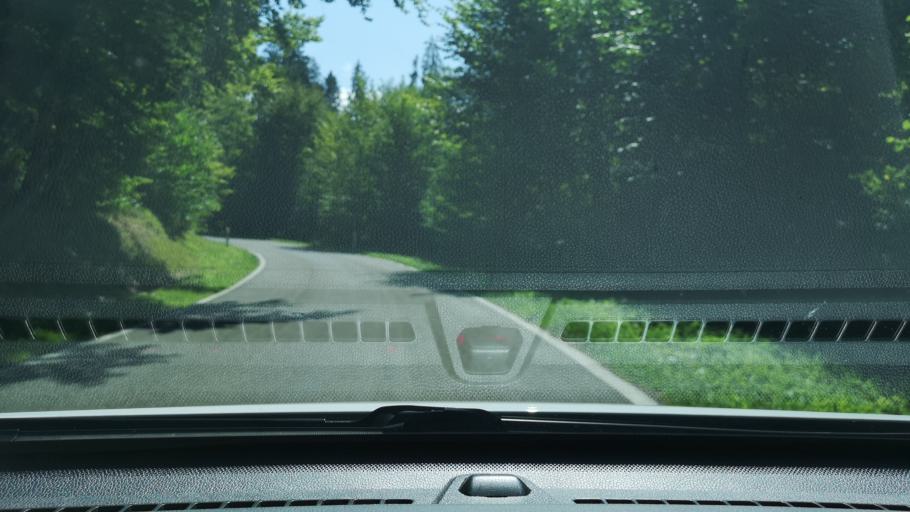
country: DE
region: Baden-Wuerttemberg
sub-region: Freiburg Region
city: Muhlheim am Bach
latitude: 48.3553
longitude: 8.7149
